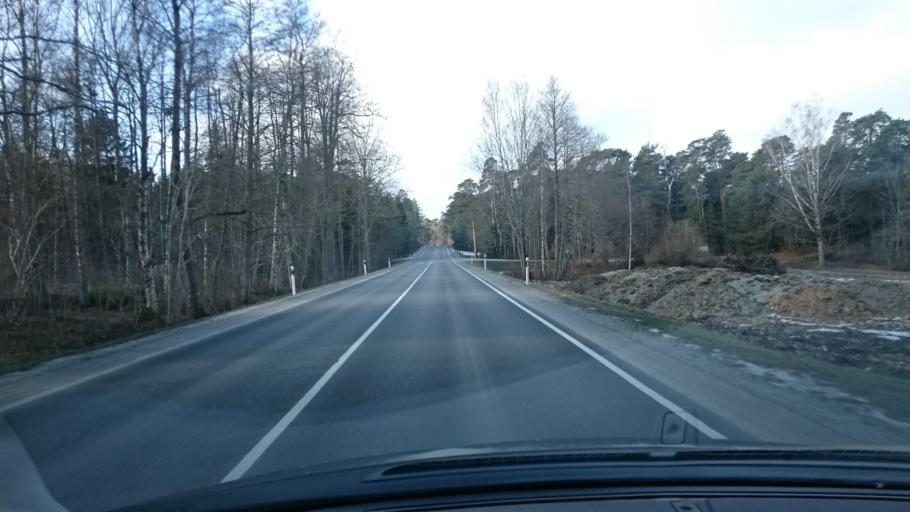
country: EE
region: Harju
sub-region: Keila linn
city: Keila
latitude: 59.3975
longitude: 24.2682
